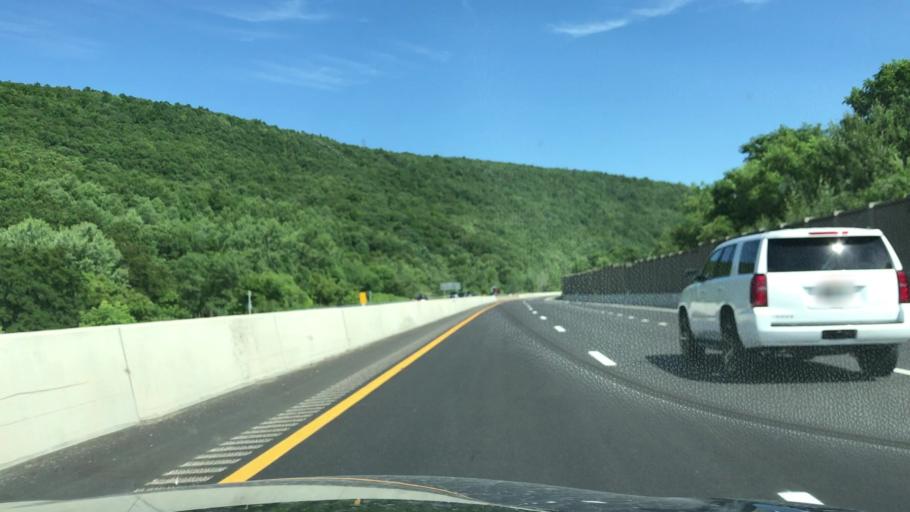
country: US
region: New York
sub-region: Steuben County
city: Corning
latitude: 42.1529
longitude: -77.0472
